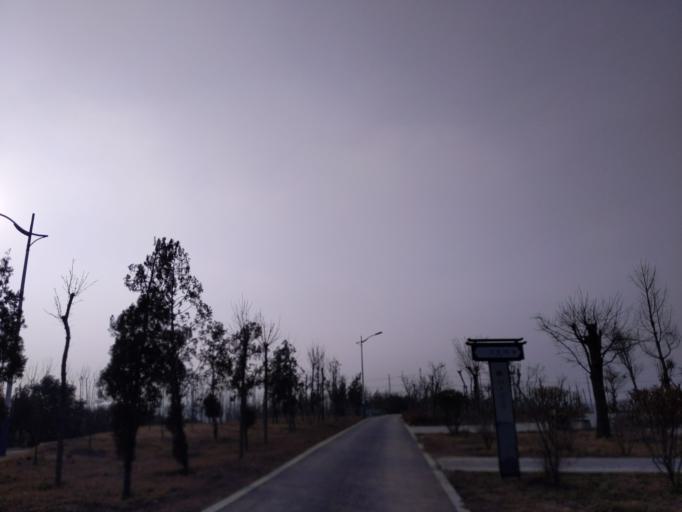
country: CN
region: Henan Sheng
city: Puyang
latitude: 35.8200
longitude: 115.0044
